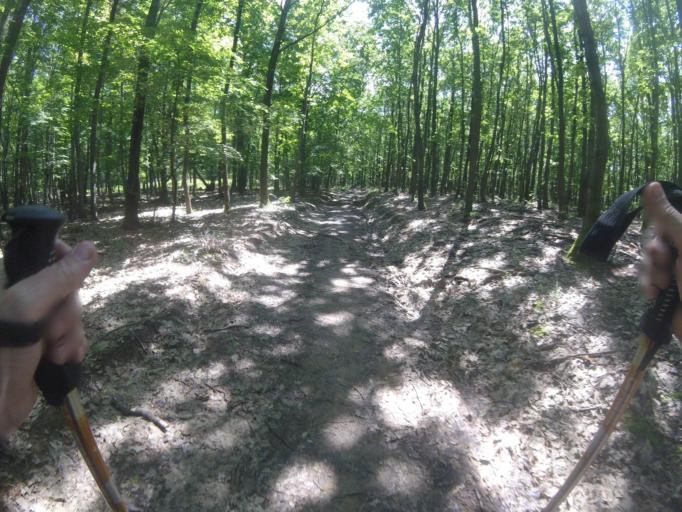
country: HU
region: Nograd
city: Matraverebely
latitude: 47.9303
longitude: 19.7990
